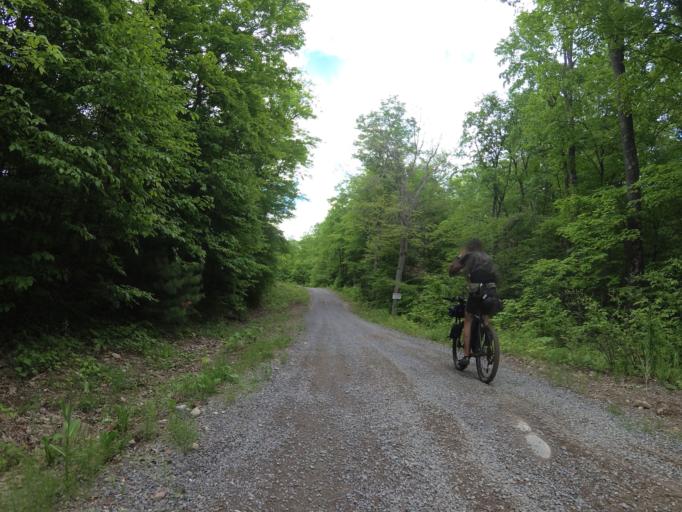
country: CA
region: Ontario
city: Renfrew
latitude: 45.1168
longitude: -76.8859
